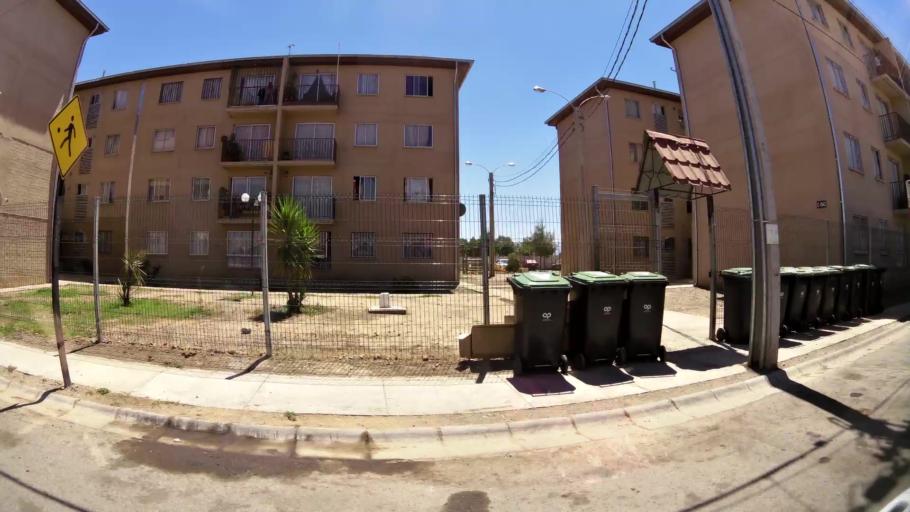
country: CL
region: O'Higgins
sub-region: Provincia de Cachapoal
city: Rancagua
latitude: -34.1515
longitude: -70.7534
